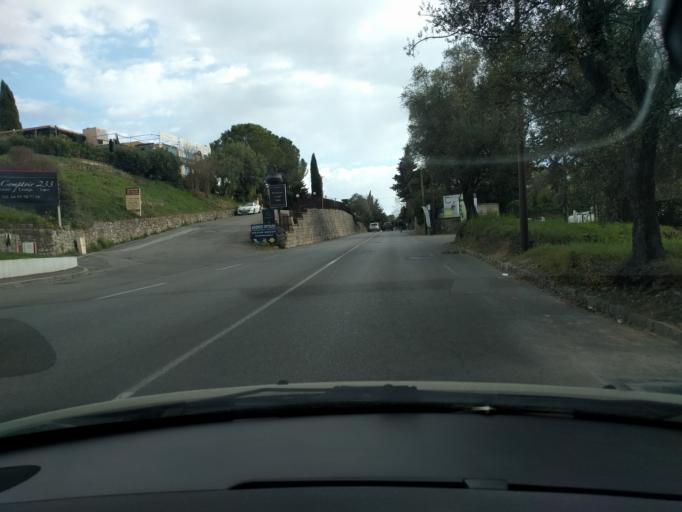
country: FR
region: Provence-Alpes-Cote d'Azur
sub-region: Departement des Alpes-Maritimes
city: Mouans-Sartoux
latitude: 43.6302
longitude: 6.9587
